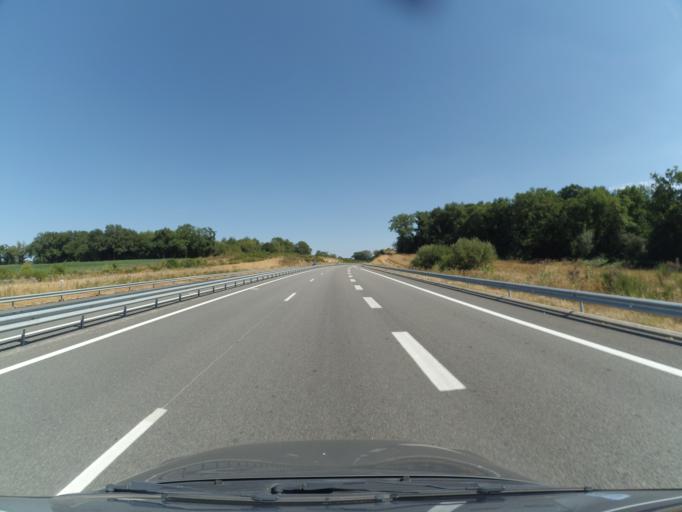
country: FR
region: Limousin
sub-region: Departement de la Haute-Vienne
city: Veyrac
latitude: 45.8825
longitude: 1.0985
